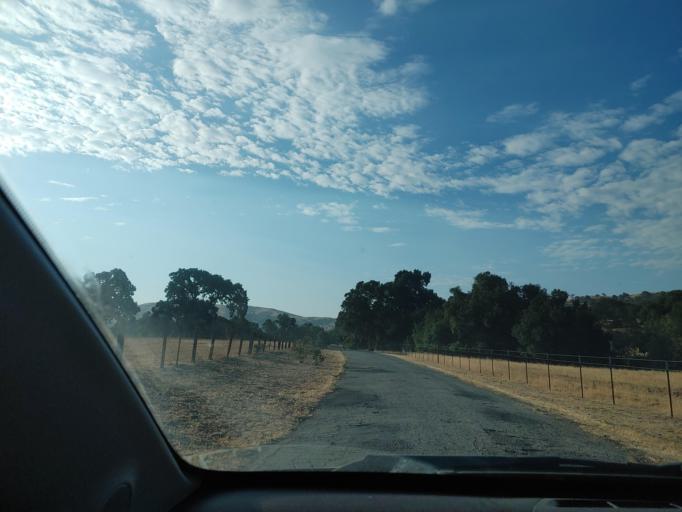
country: US
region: California
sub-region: San Benito County
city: Ridgemark
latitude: 36.7793
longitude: -121.2434
